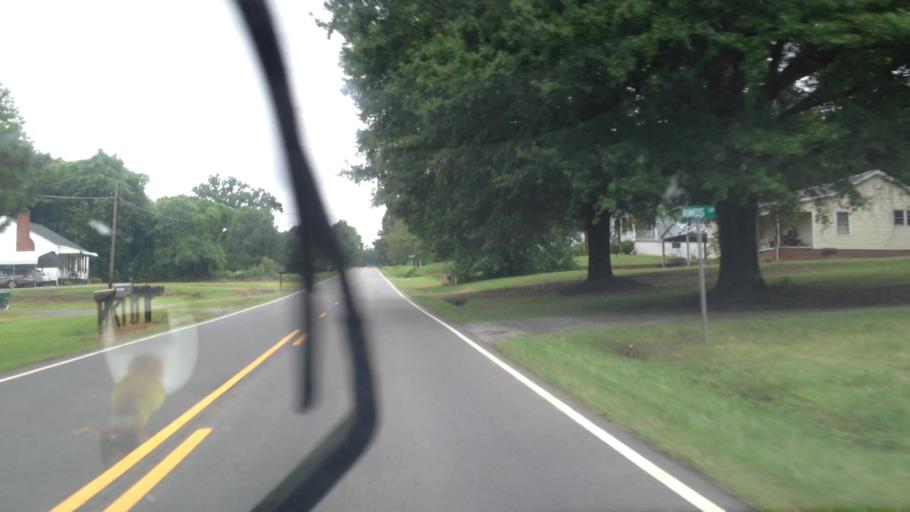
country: US
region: North Carolina
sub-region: Rockingham County
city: Mayodan
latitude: 36.4096
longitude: -79.9955
